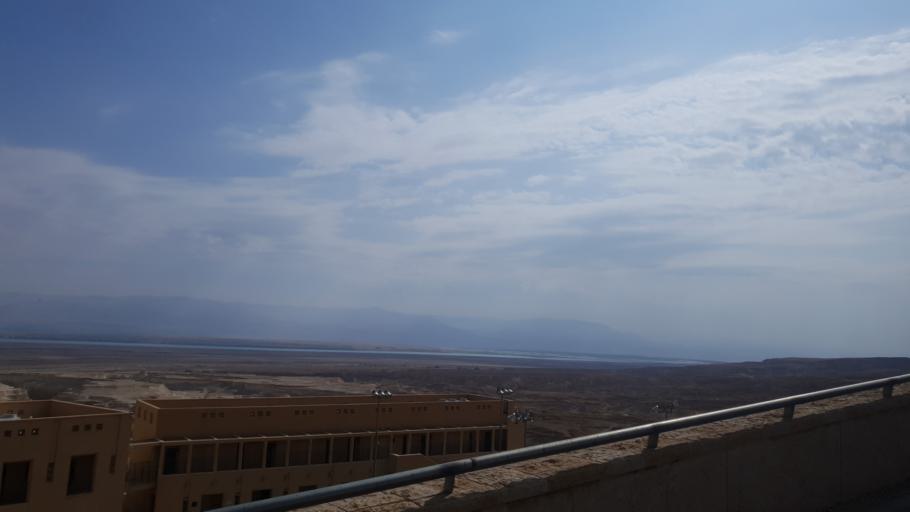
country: IL
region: Southern District
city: `En Boqeq
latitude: 31.3103
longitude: 35.3632
